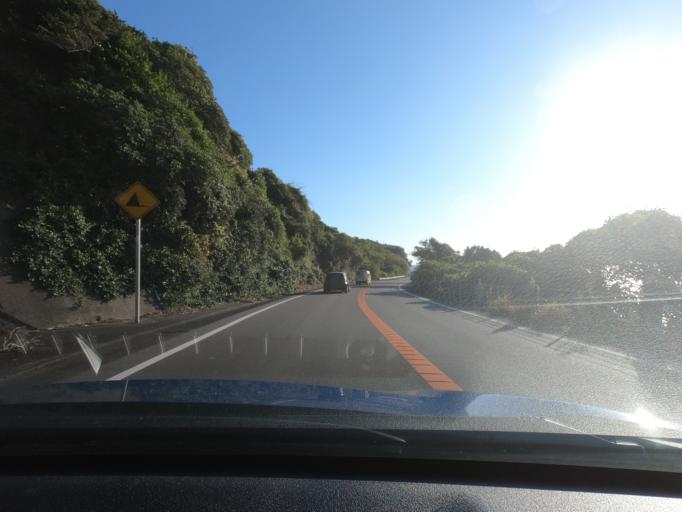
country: JP
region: Kagoshima
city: Akune
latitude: 31.9527
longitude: 130.2165
